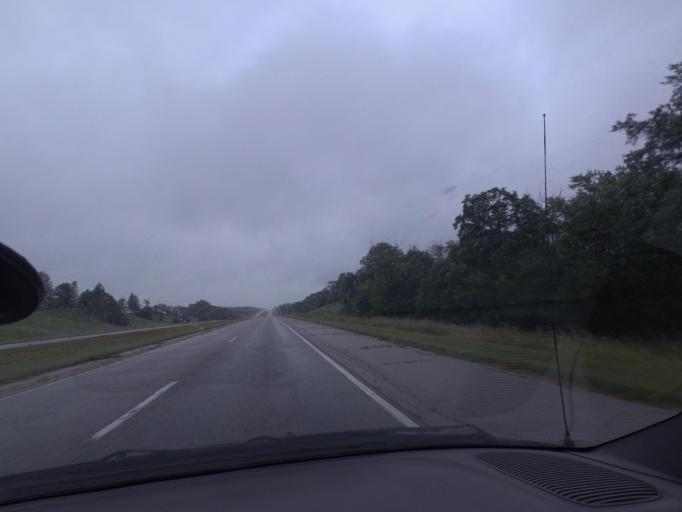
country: US
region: Illinois
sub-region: Pike County
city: Barry
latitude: 39.6926
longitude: -90.9464
